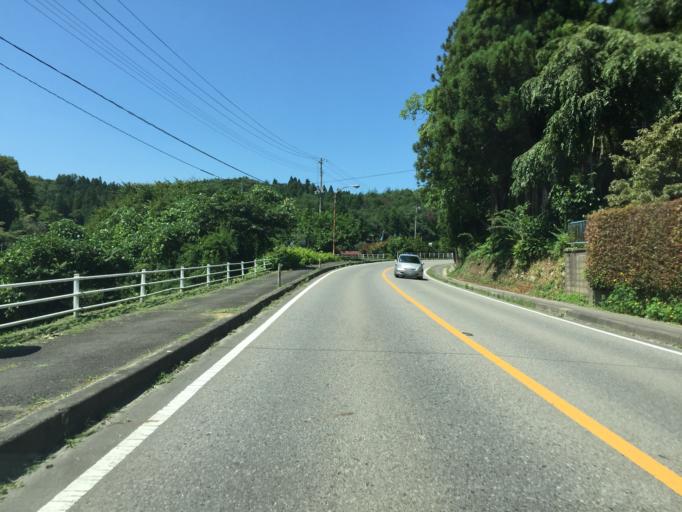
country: JP
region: Fukushima
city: Nihommatsu
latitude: 37.6387
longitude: 140.4639
